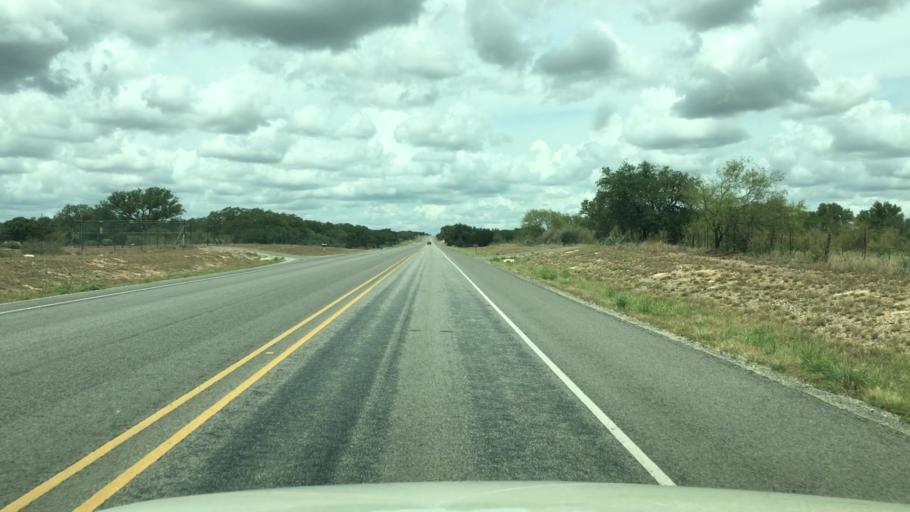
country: US
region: Texas
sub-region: McCulloch County
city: Brady
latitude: 31.0239
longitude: -99.2198
